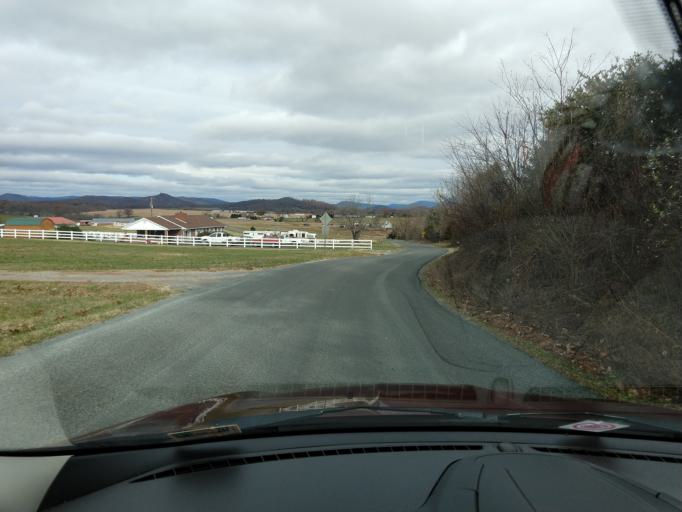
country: US
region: Virginia
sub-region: Franklin County
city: North Shore
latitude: 37.2218
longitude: -79.6795
